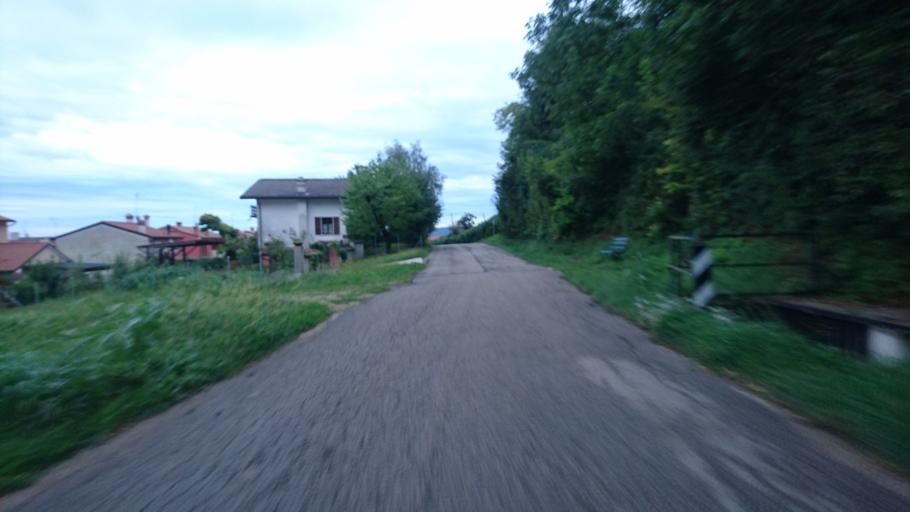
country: IT
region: Veneto
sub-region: Provincia di Treviso
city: Mosnigo
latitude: 45.8966
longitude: 12.0798
